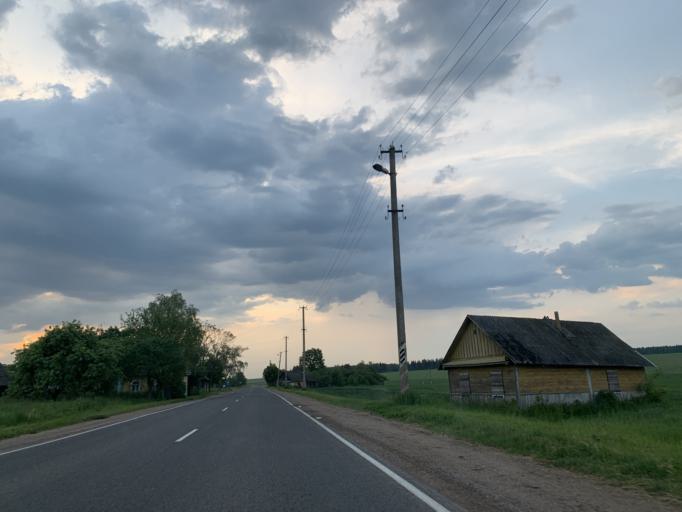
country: BY
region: Minsk
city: Tsimkavichy
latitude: 53.1313
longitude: 26.8757
